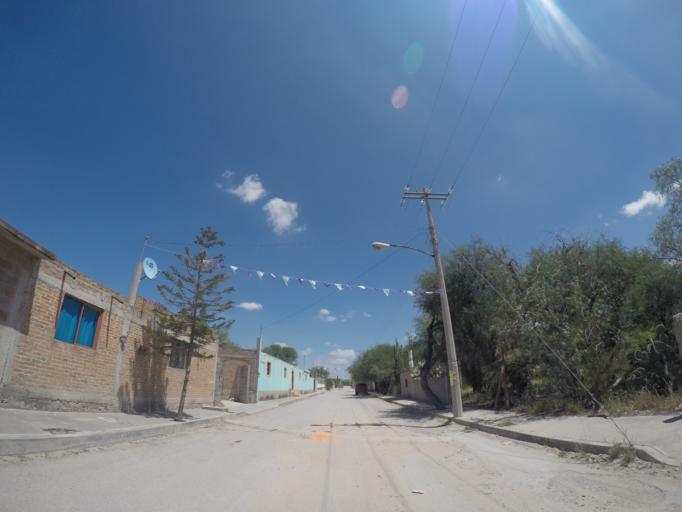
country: MX
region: San Luis Potosi
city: La Pila
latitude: 21.9991
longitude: -100.8982
